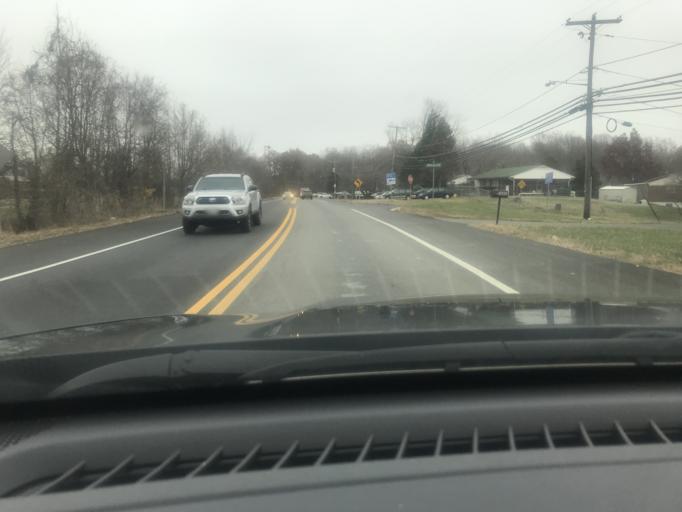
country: US
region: Maryland
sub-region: Prince George's County
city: Friendly
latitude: 38.7723
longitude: -76.9655
